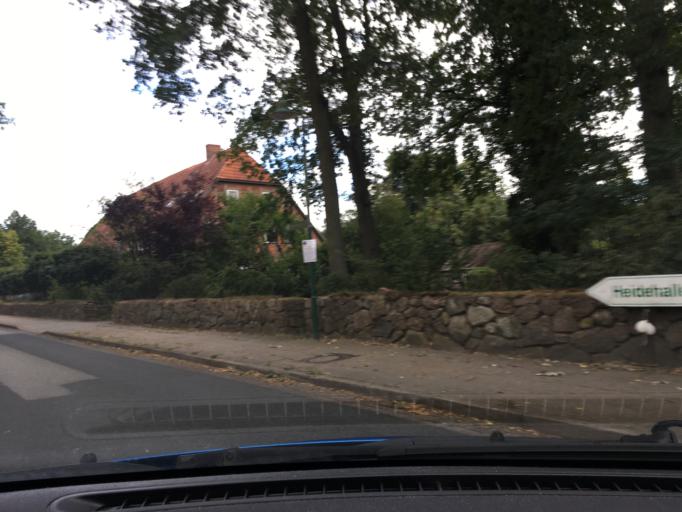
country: DE
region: Lower Saxony
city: Undeloh
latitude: 53.2295
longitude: 9.9174
